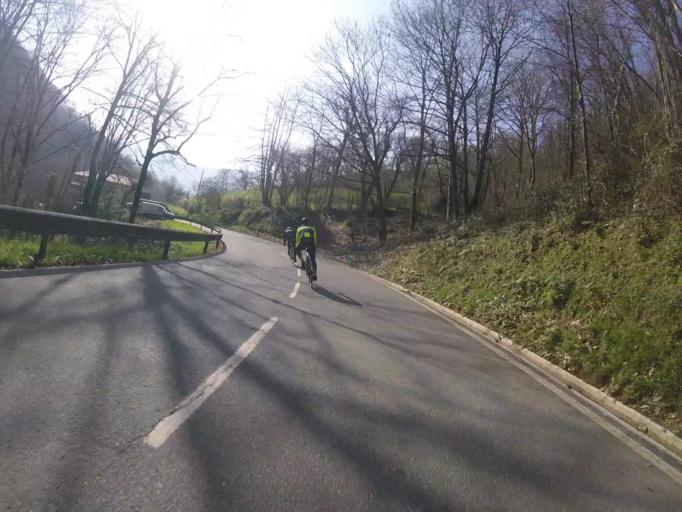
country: ES
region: Navarre
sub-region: Provincia de Navarra
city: Bera
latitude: 43.2866
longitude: -1.6801
